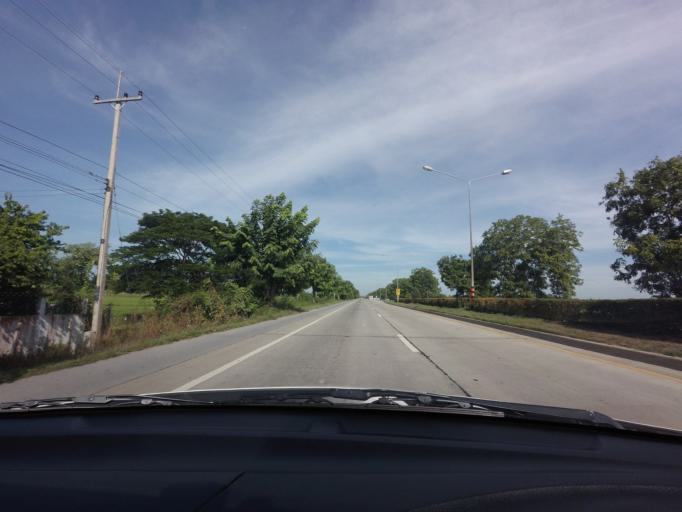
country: TH
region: Suphan Buri
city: Suphan Buri
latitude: 14.4553
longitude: 100.0717
